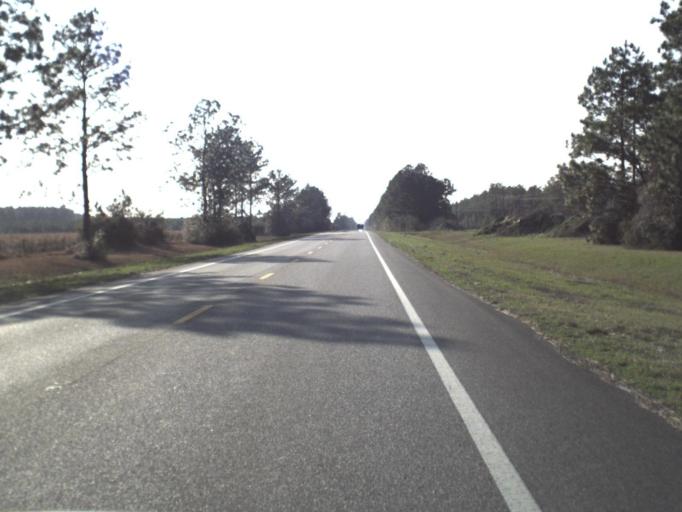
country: US
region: Florida
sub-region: Bay County
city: Lynn Haven
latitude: 30.4391
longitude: -85.7206
